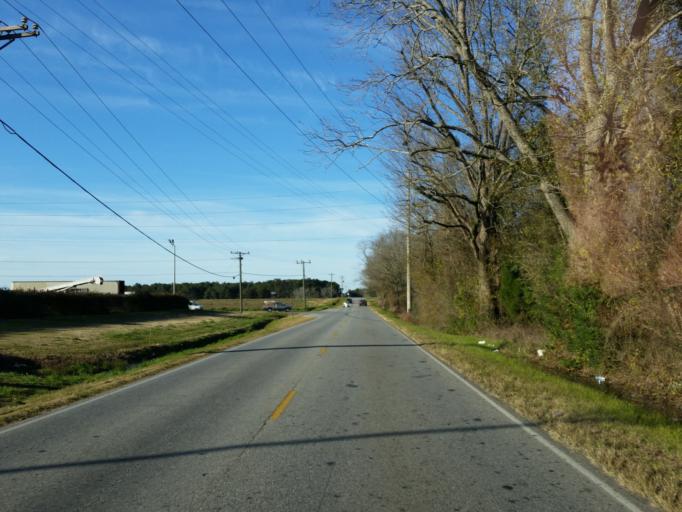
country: US
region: Georgia
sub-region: Lowndes County
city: Hahira
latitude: 30.9331
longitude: -83.3498
